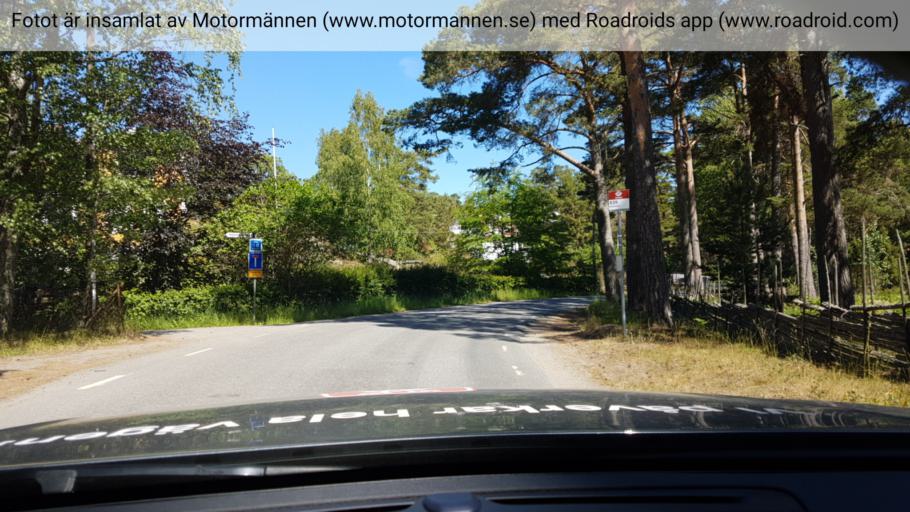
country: SE
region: Stockholm
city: Dalaro
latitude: 59.1444
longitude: 18.4348
